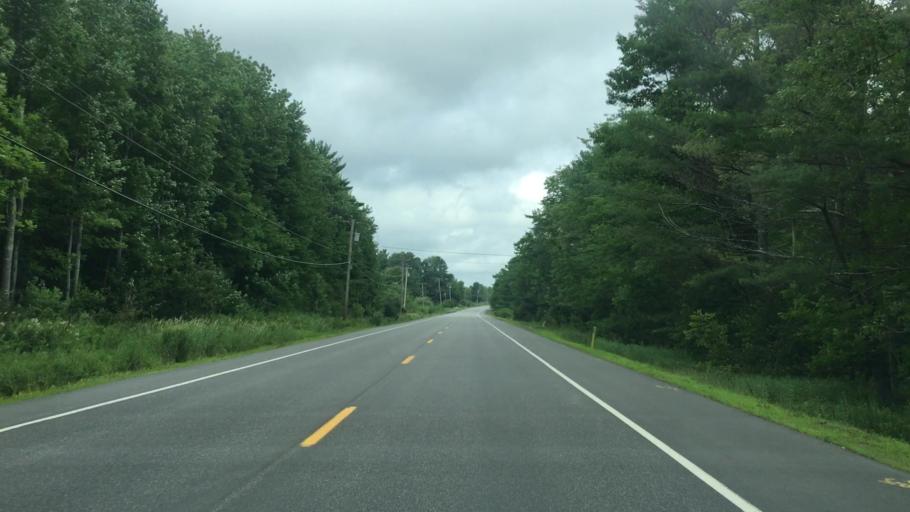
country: US
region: Maine
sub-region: Kennebec County
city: Pittston
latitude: 44.2072
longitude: -69.7544
